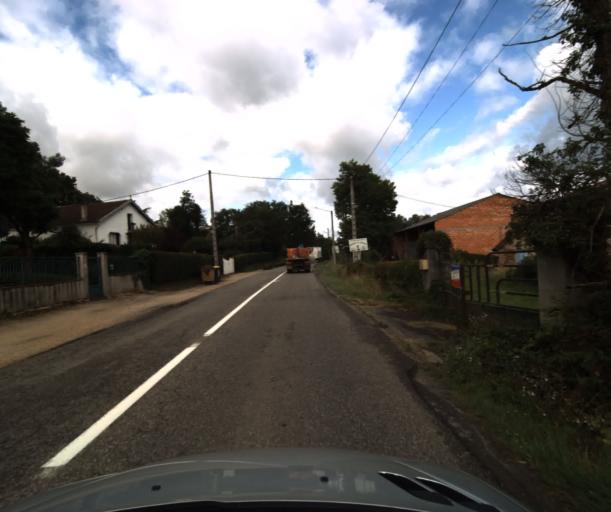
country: FR
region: Midi-Pyrenees
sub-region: Departement du Tarn-et-Garonne
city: Saint-Nicolas-de-la-Grave
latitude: 44.0303
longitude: 1.0422
